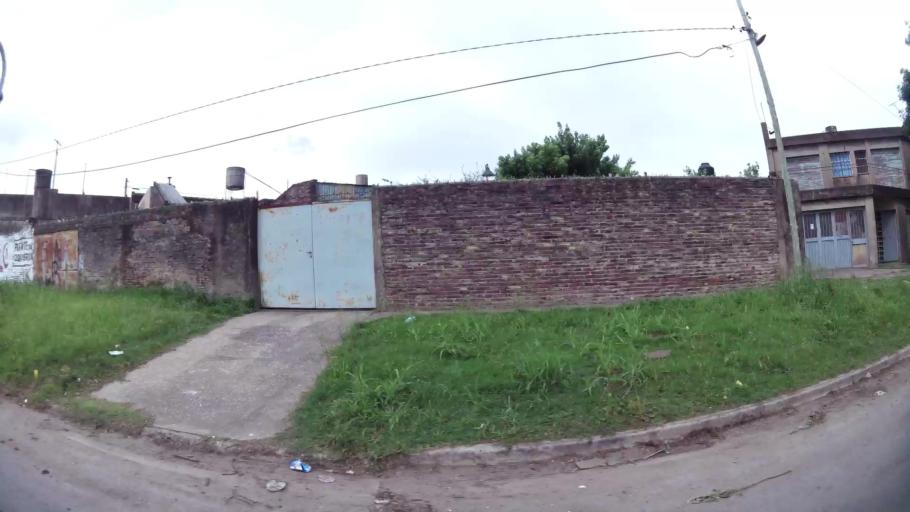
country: AR
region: Santa Fe
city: Gobernador Galvez
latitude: -33.0072
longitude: -60.6762
